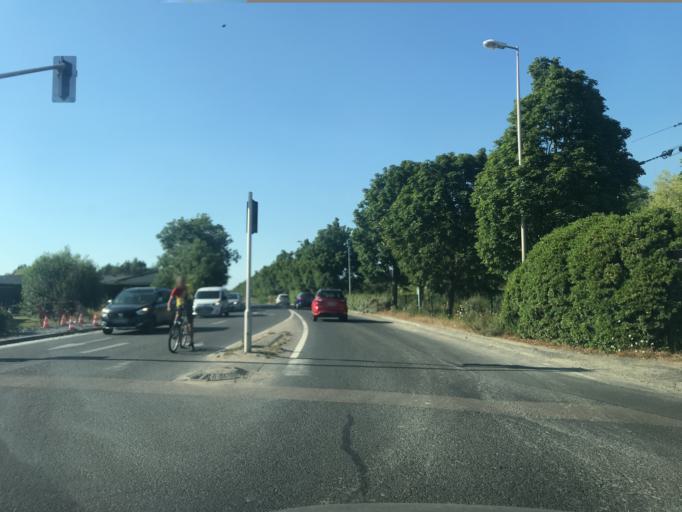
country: FR
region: Lower Normandy
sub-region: Departement du Calvados
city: Touques
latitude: 49.3493
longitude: 0.0911
